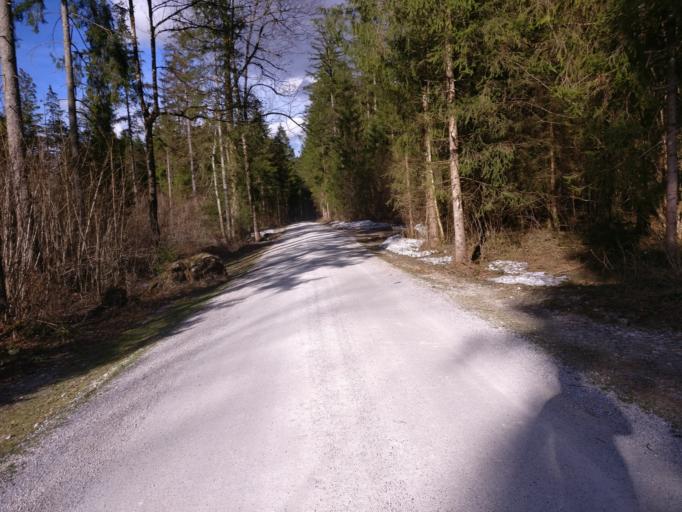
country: AT
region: Salzburg
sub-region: Politischer Bezirk Hallein
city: Golling an der Salzach
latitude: 47.5805
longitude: 13.1472
